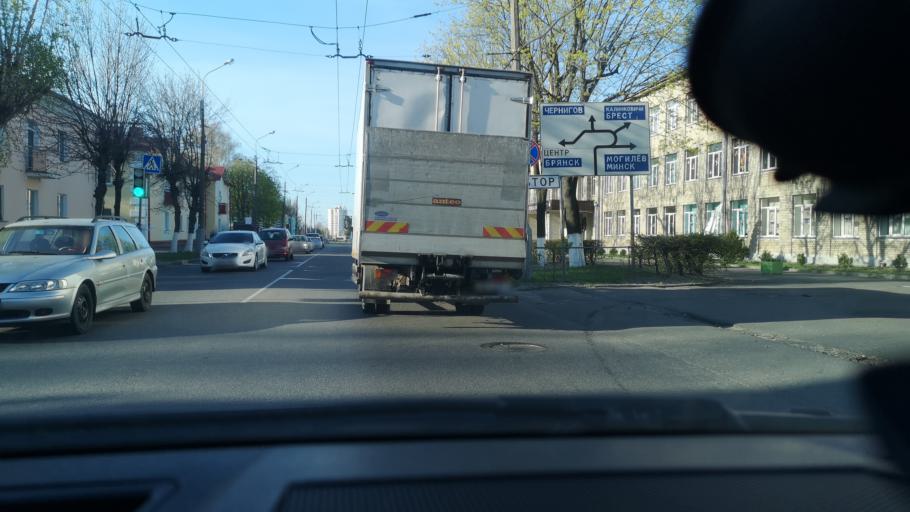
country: BY
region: Gomel
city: Gomel
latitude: 52.4215
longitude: 30.9730
